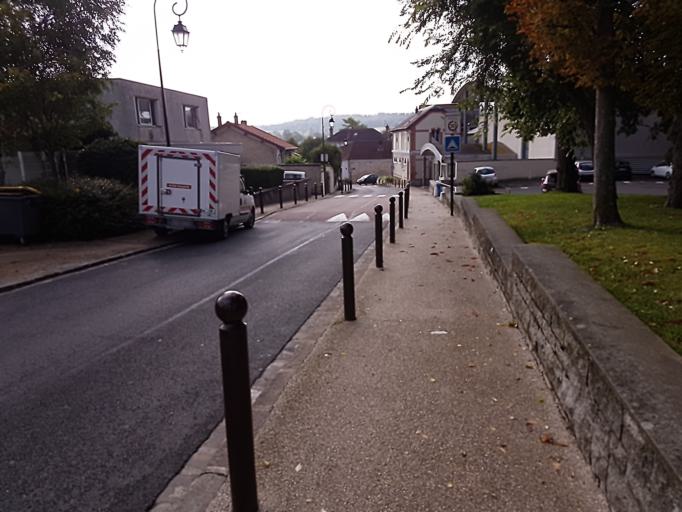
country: FR
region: Ile-de-France
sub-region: Departement de Seine-et-Marne
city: Avon
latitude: 48.4176
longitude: 2.7294
